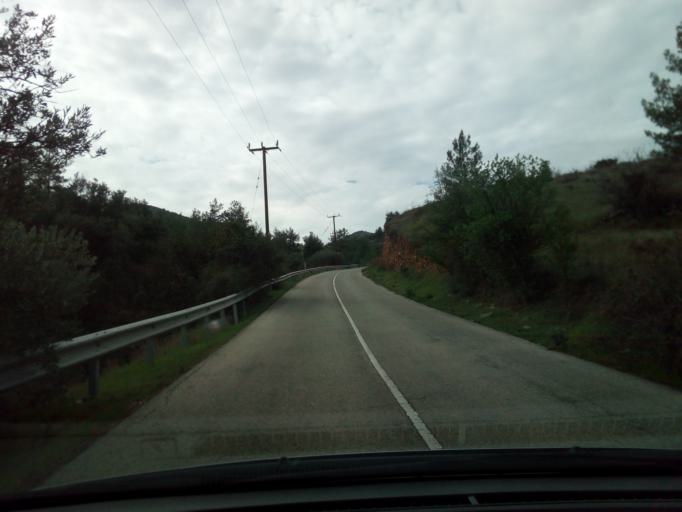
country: CY
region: Lefkosia
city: Klirou
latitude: 34.9781
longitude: 33.1827
